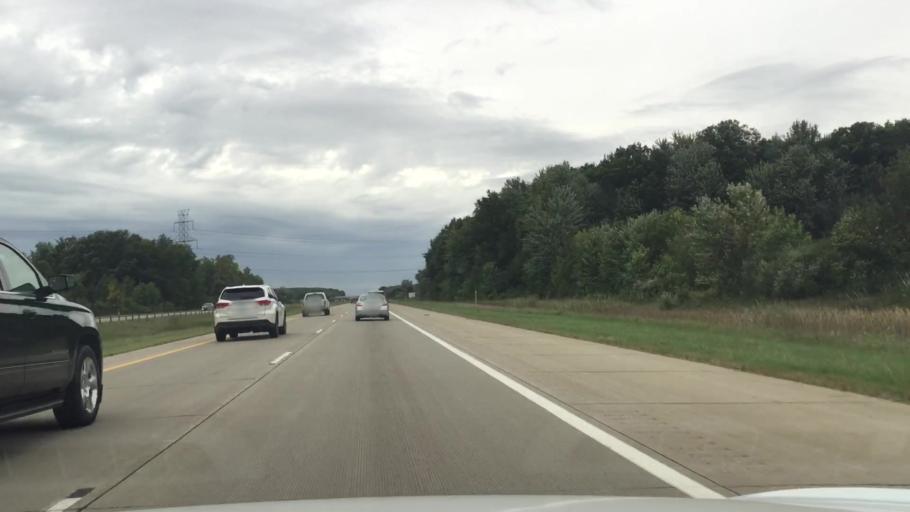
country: US
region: Michigan
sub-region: Macomb County
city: Richmond
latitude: 42.7738
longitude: -82.6814
